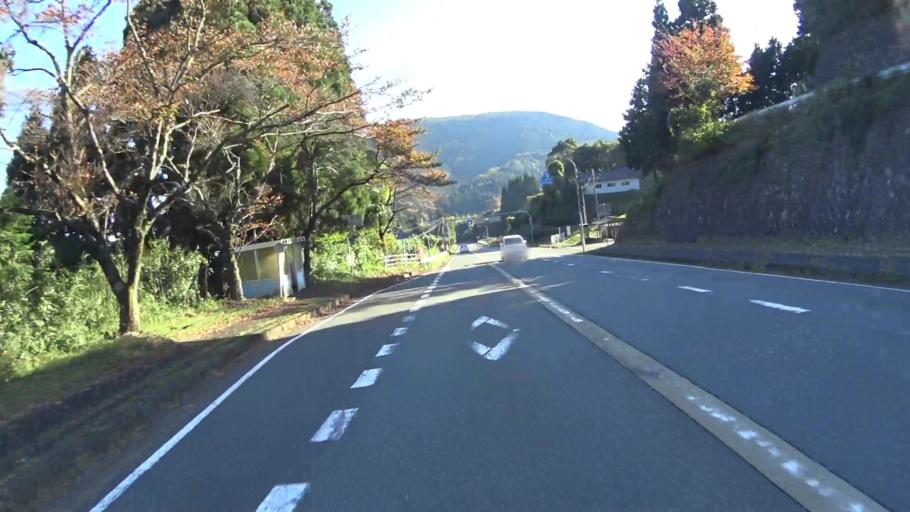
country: JP
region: Kyoto
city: Fukuchiyama
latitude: 35.4045
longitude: 135.0822
